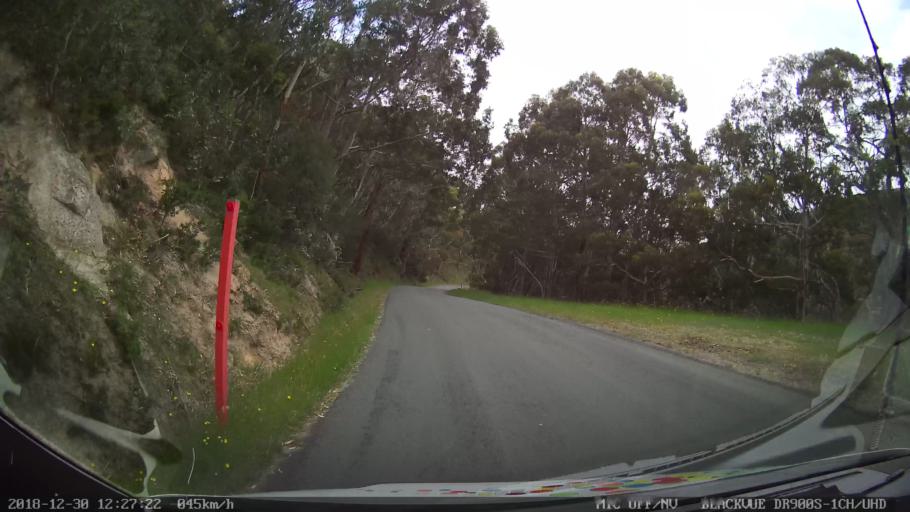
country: AU
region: New South Wales
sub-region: Snowy River
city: Jindabyne
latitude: -36.3315
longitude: 148.4902
